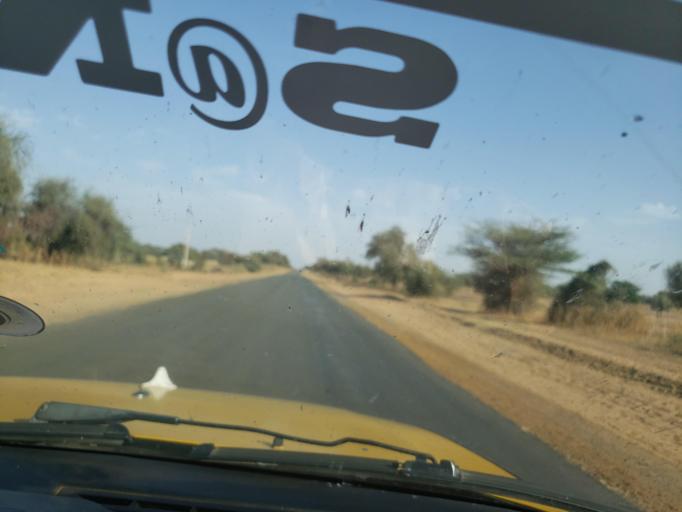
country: SN
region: Louga
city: Louga
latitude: 15.5041
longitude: -15.9534
